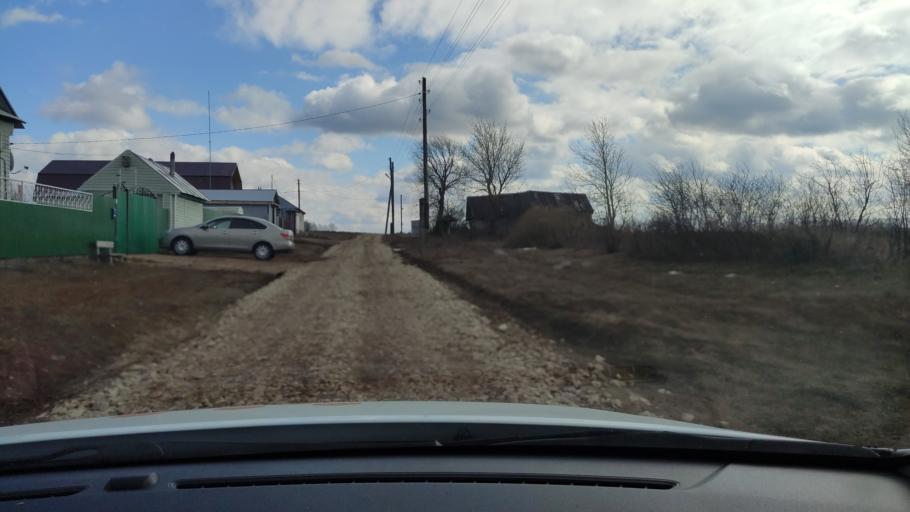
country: RU
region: Tatarstan
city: Vysokaya Gora
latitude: 56.2079
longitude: 49.3163
